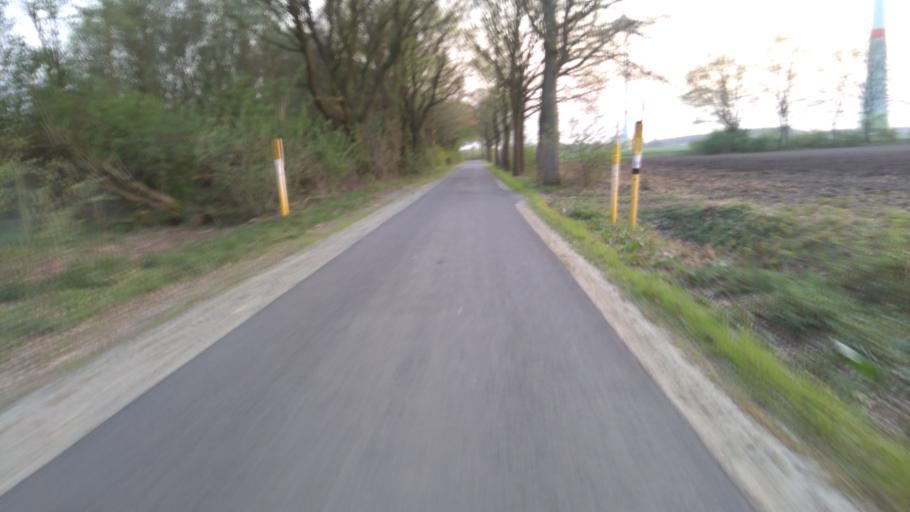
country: DE
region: Lower Saxony
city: Harsefeld
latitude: 53.4914
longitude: 9.4877
